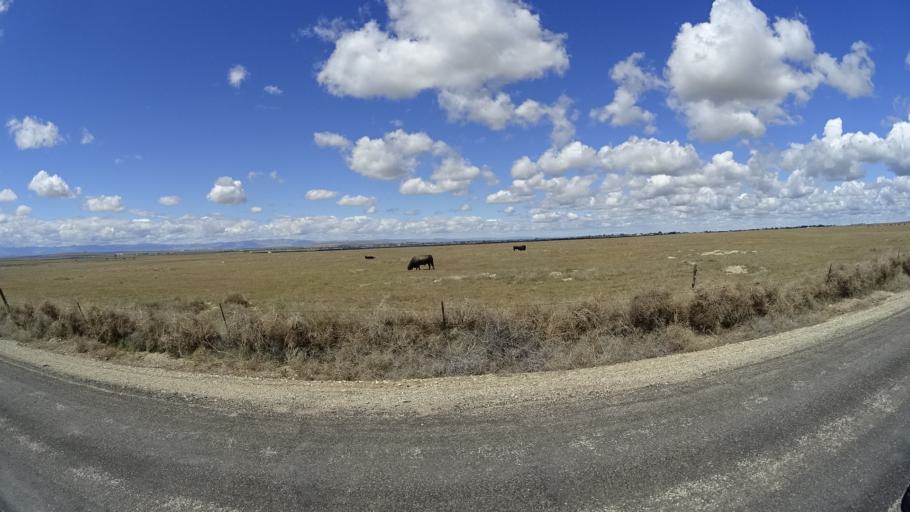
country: US
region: Idaho
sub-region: Ada County
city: Kuna
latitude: 43.4683
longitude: -116.2744
